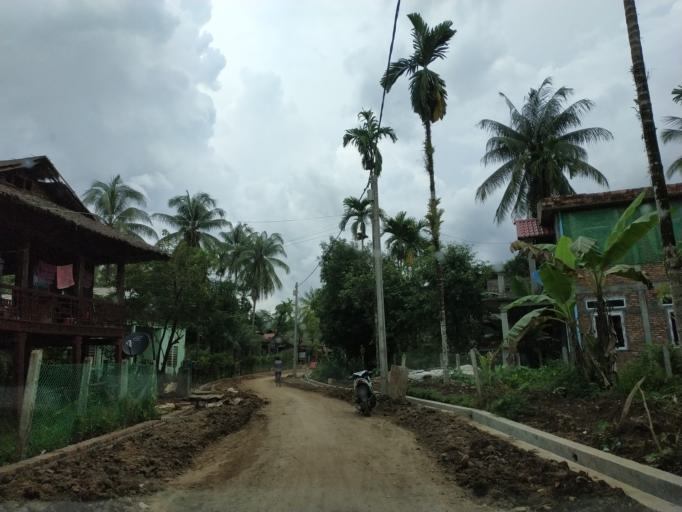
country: MM
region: Tanintharyi
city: Dawei
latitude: 13.8607
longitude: 98.2663
